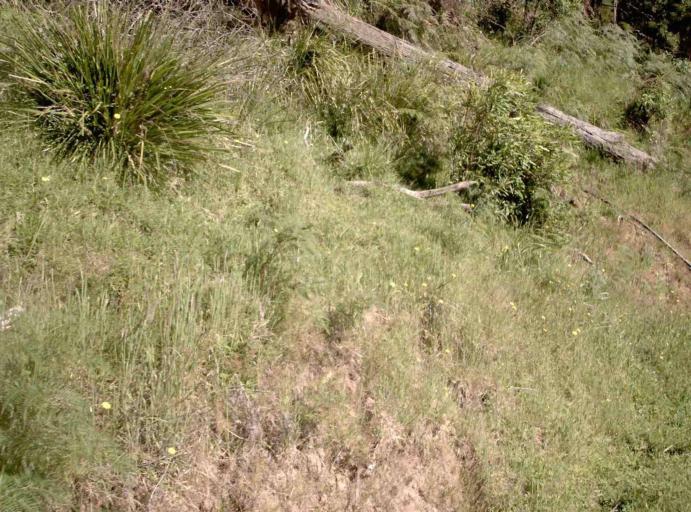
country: AU
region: New South Wales
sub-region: Bombala
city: Bombala
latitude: -37.3458
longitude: 148.6933
